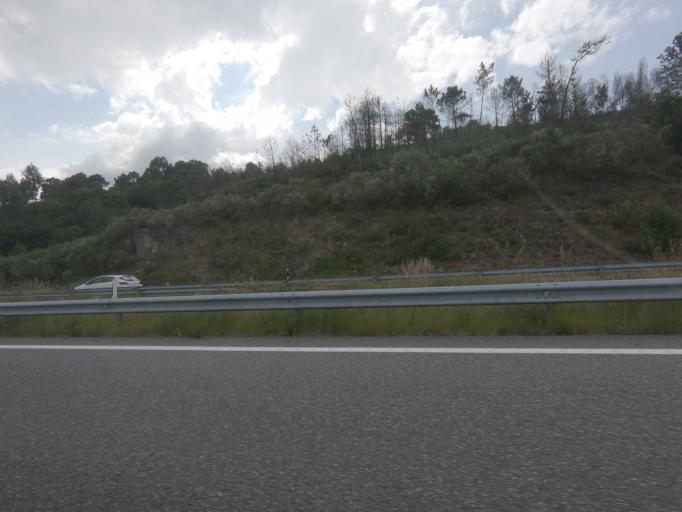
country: ES
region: Galicia
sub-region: Provincia de Ourense
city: Melon
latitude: 42.2459
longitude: -8.2263
